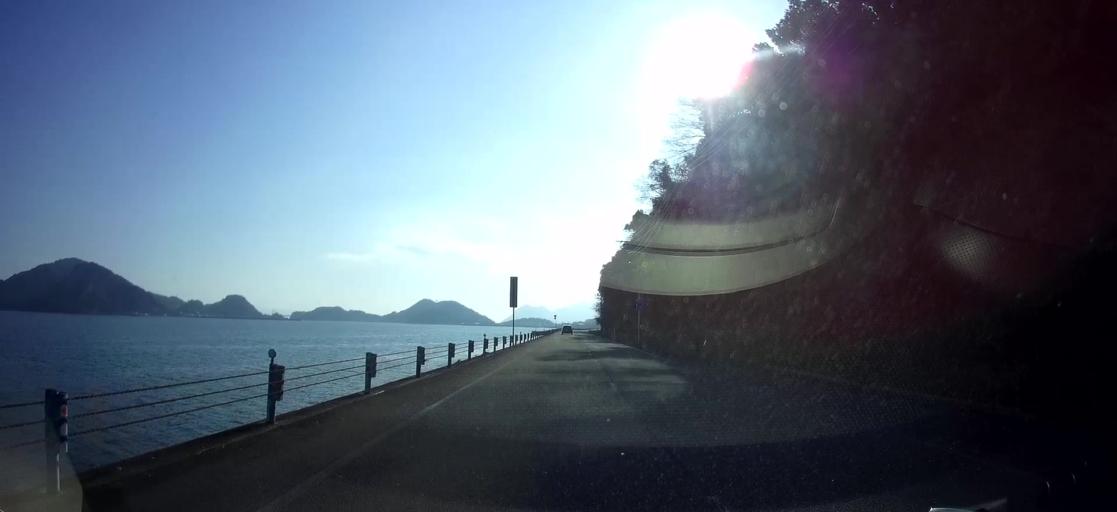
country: JP
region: Kumamoto
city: Minamata
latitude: 32.4131
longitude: 130.4099
